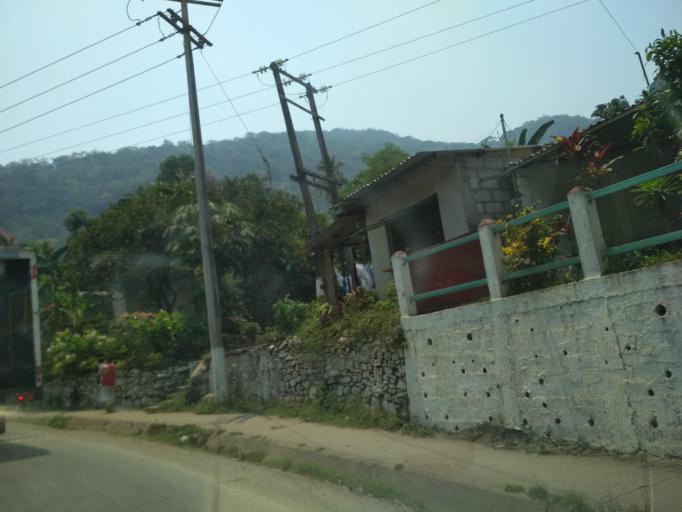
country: MX
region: Veracruz
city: Cosolapa
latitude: 18.5975
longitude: -96.6901
